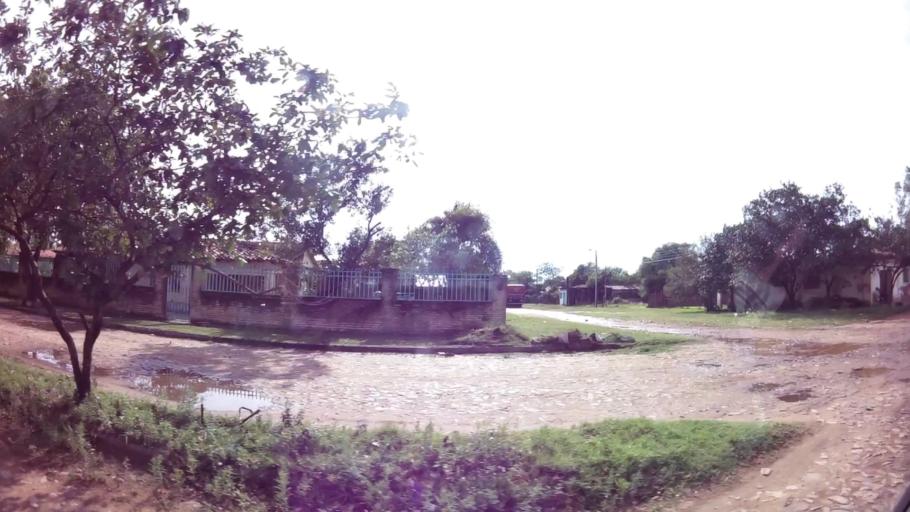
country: PY
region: Central
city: Limpio
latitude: -25.1690
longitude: -57.4894
